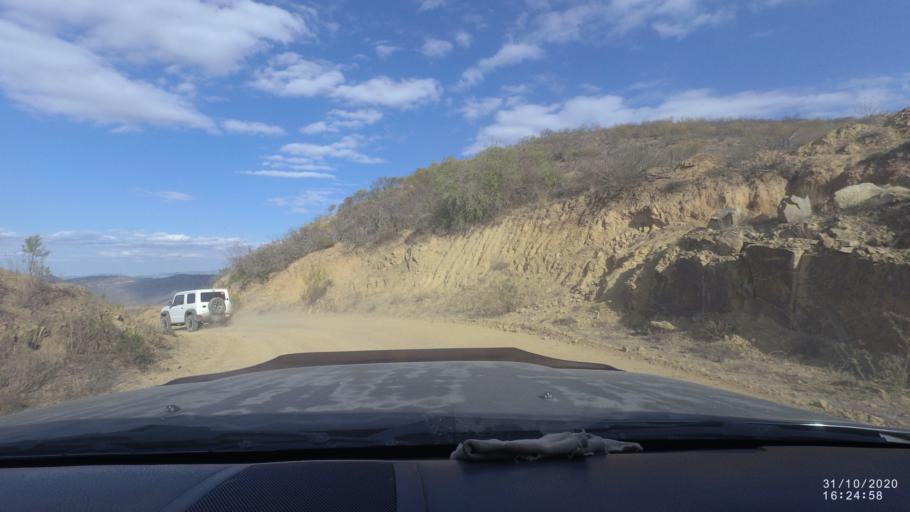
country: BO
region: Chuquisaca
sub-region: Provincia Zudanez
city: Mojocoya
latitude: -18.4036
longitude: -64.5884
